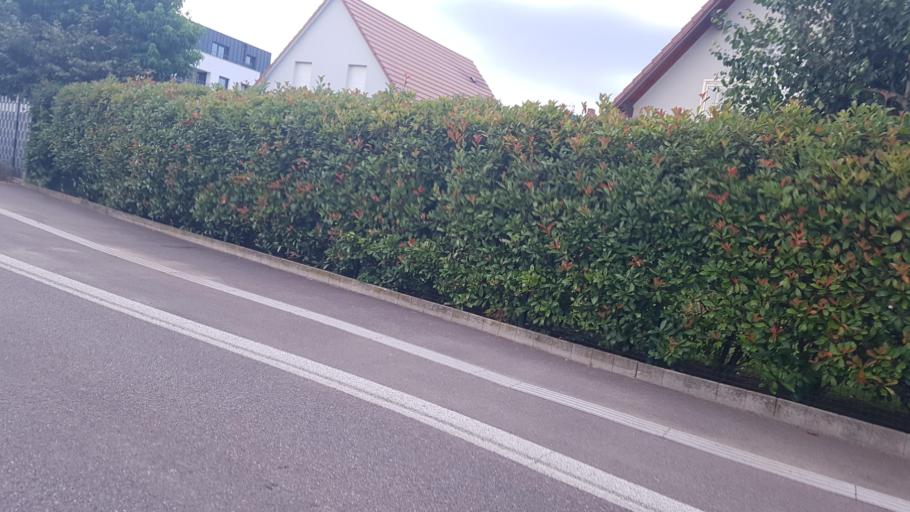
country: FR
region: Alsace
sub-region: Departement du Bas-Rhin
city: Brumath
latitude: 48.7270
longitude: 7.7224
